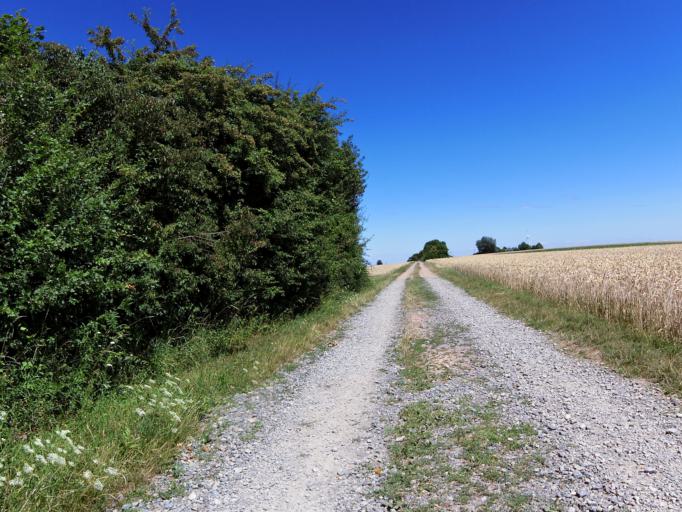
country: DE
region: Bavaria
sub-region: Regierungsbezirk Unterfranken
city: Gerbrunn
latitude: 49.7695
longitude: 10.0138
